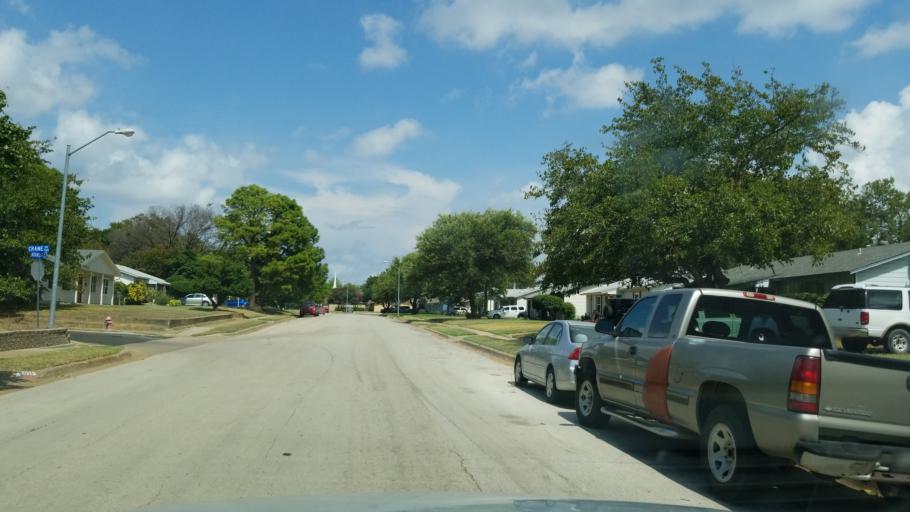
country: US
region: Texas
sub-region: Tarrant County
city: Euless
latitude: 32.8490
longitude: -97.0903
